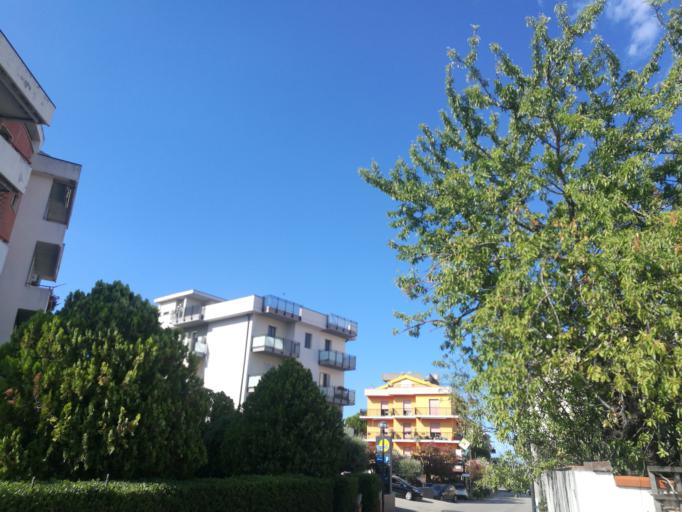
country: IT
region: Molise
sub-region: Provincia di Campobasso
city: Termoli
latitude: 41.9925
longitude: 14.9961
